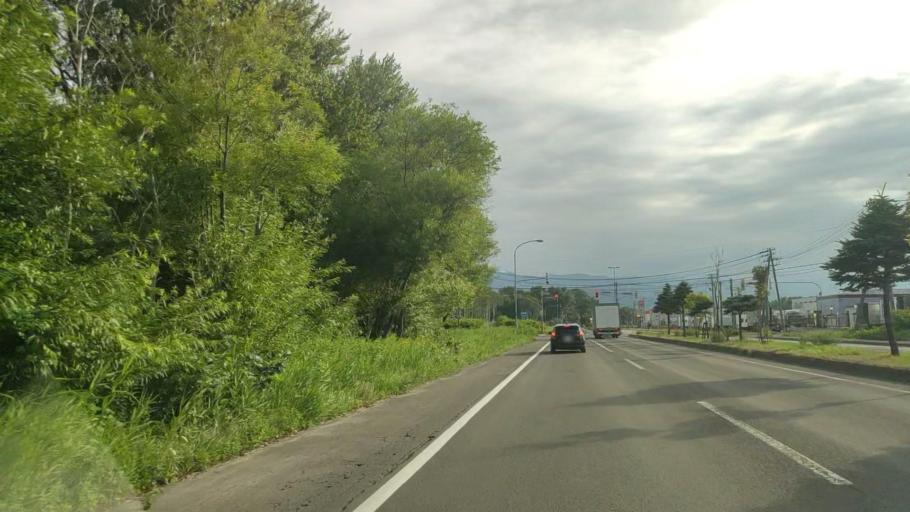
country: JP
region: Hokkaido
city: Ishikari
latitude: 43.1621
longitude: 141.2843
